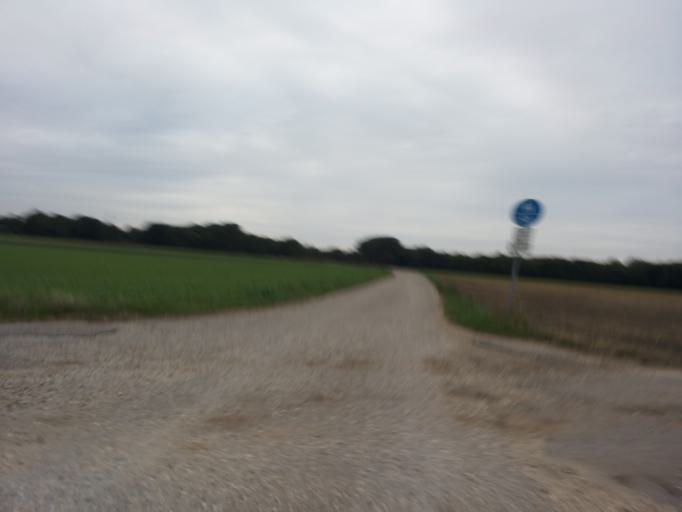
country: DE
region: Bavaria
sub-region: Upper Bavaria
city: Weichering
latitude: 48.7501
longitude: 11.3659
